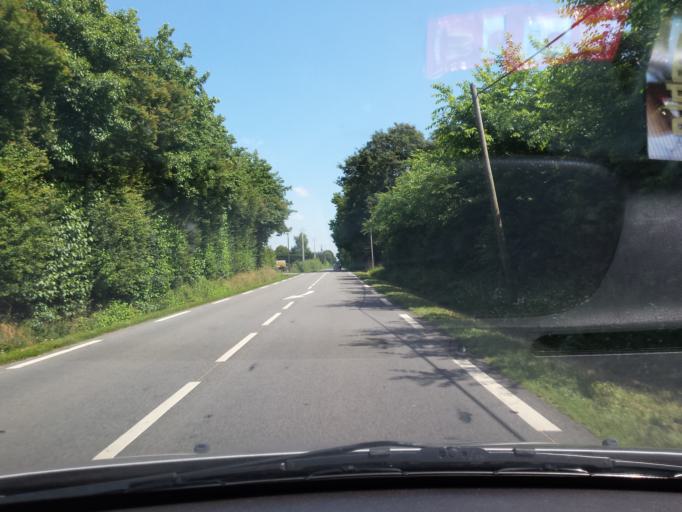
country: FR
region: Pays de la Loire
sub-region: Departement de la Loire-Atlantique
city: Machecoul
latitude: 47.0070
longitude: -1.8430
